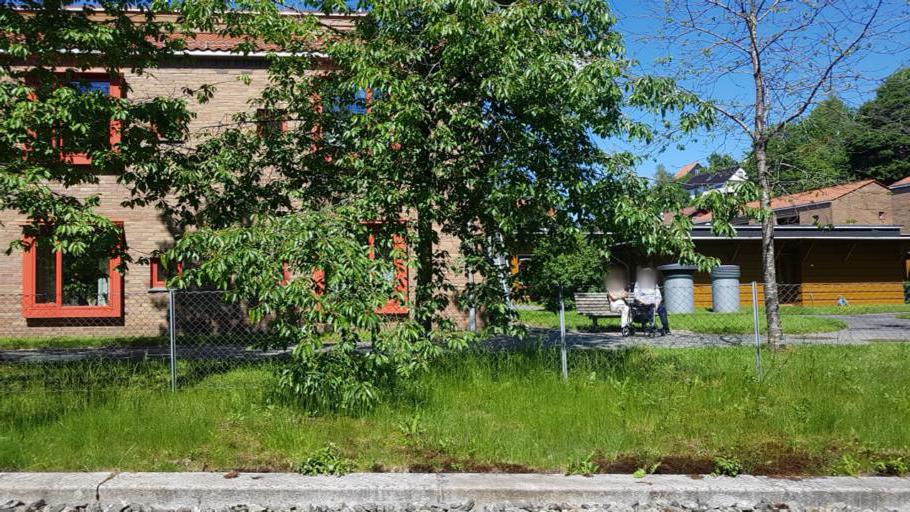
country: NO
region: Hordaland
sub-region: Bergen
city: Bergen
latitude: 60.3470
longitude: 5.3529
